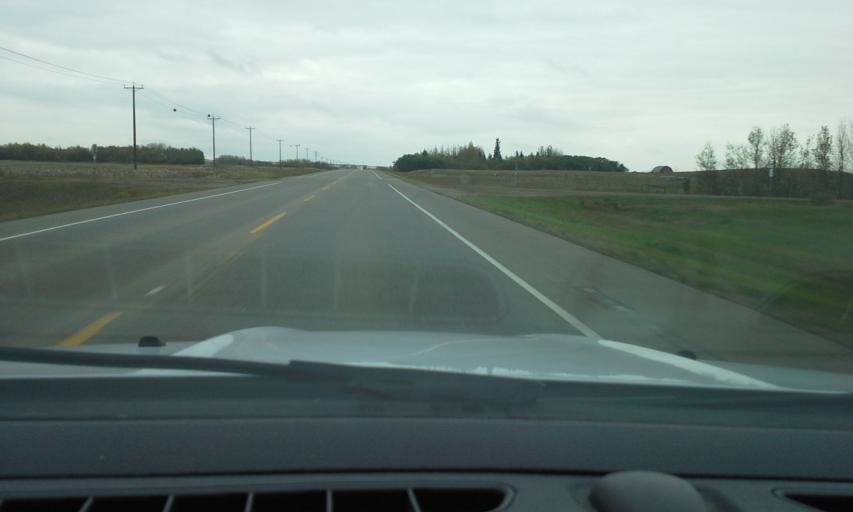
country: CA
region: Saskatchewan
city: Lloydminster
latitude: 53.2780
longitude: -109.8341
